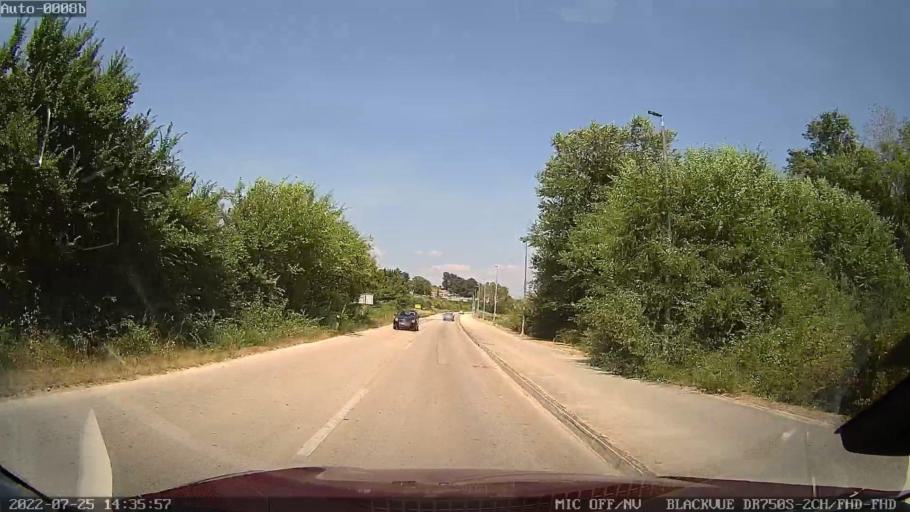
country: HR
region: Zadarska
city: Galovac
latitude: 44.1076
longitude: 15.3814
